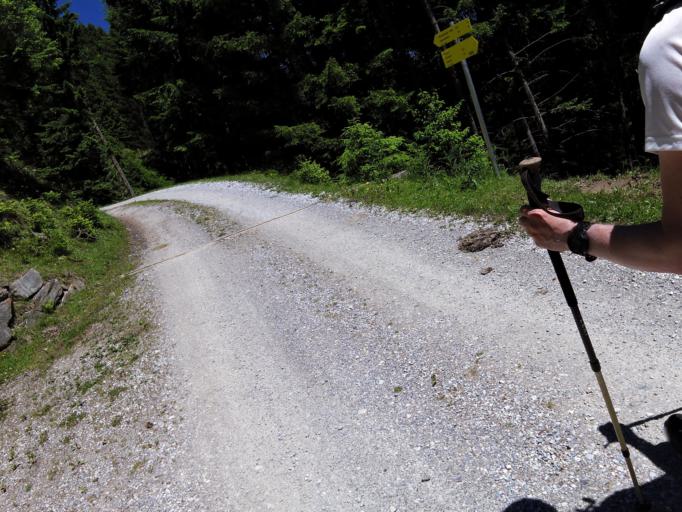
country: AT
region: Tyrol
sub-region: Politischer Bezirk Innsbruck Land
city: Neustift im Stubaital
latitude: 47.1123
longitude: 11.2908
